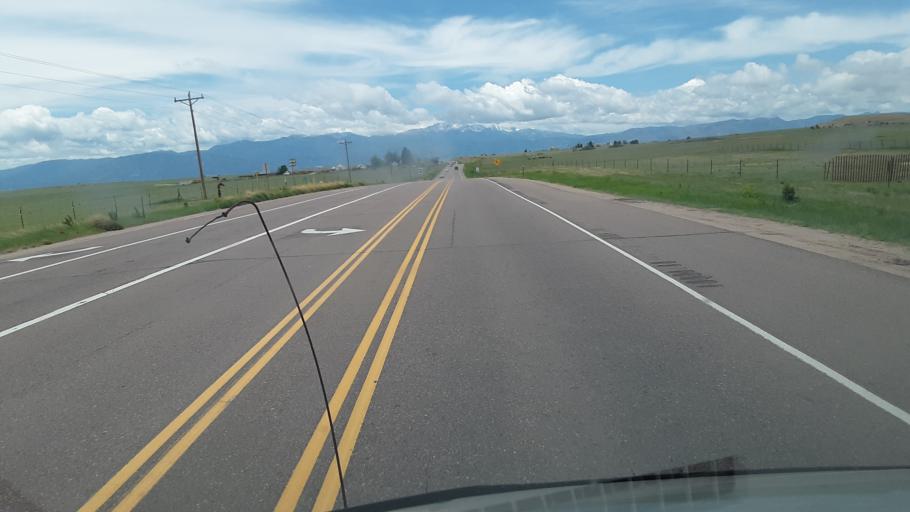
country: US
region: Colorado
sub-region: El Paso County
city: Cimarron Hills
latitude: 38.8387
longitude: -104.5543
